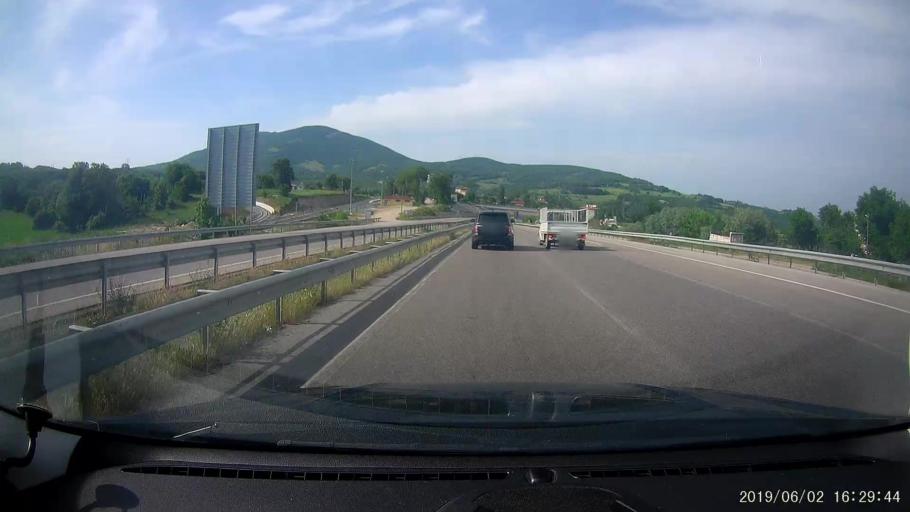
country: TR
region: Samsun
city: Ladik
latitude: 41.0165
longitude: 35.8722
